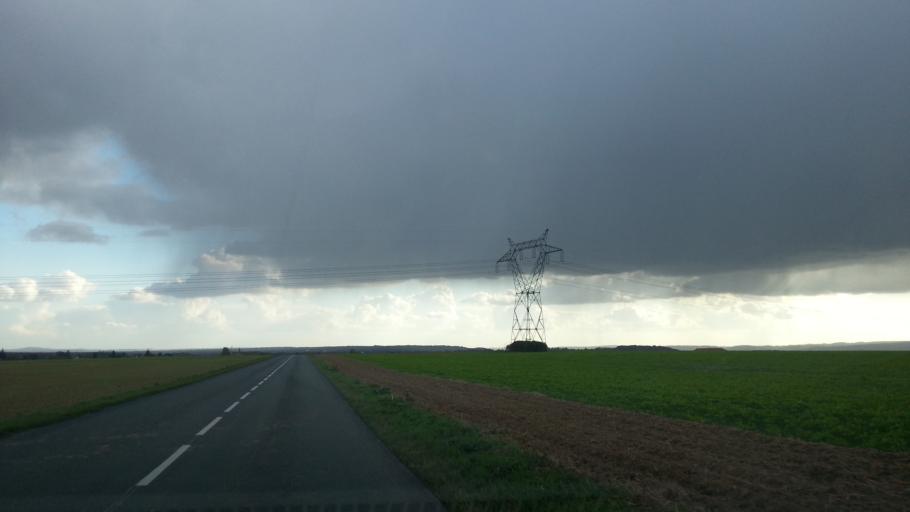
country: FR
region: Picardie
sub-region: Departement de l'Oise
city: Villers-sous-Saint-Leu
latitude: 49.2321
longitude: 2.4117
